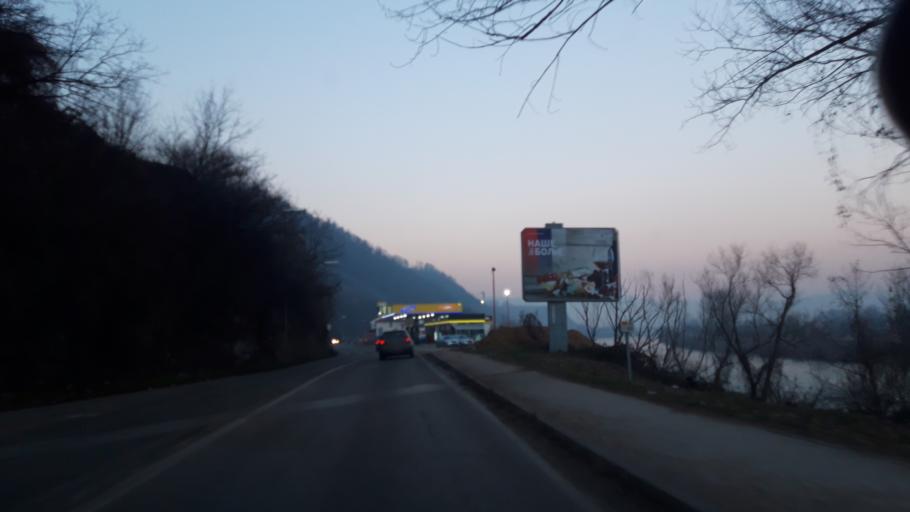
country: BA
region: Republika Srpska
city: Zvornik
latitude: 44.3949
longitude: 19.1068
